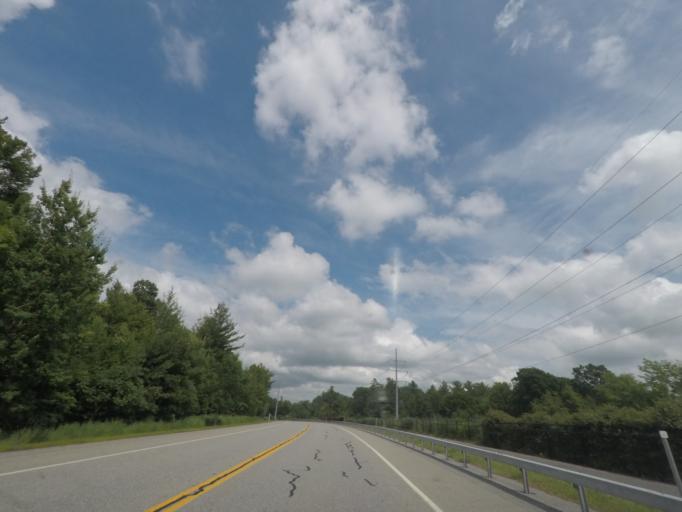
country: US
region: New York
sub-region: Saratoga County
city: Country Knolls
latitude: 42.9584
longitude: -73.7722
